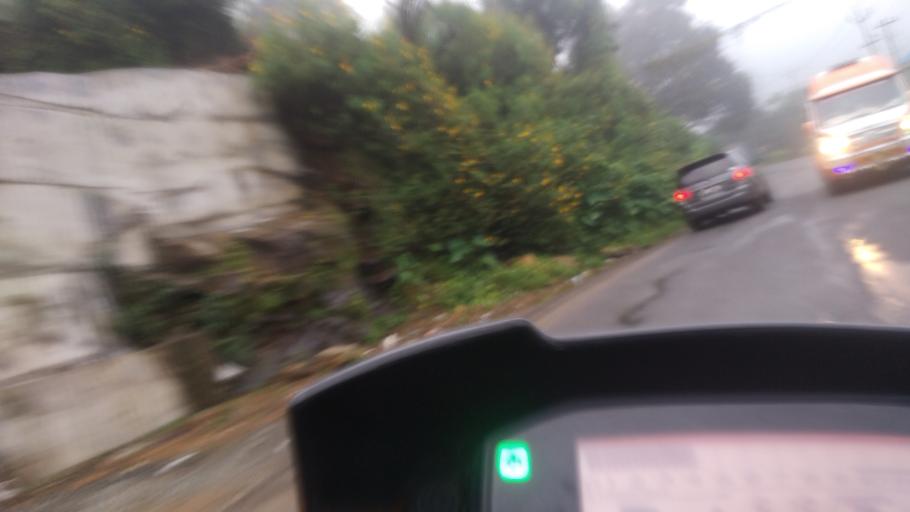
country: IN
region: Kerala
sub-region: Kottayam
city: Erattupetta
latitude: 9.5742
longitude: 76.9916
